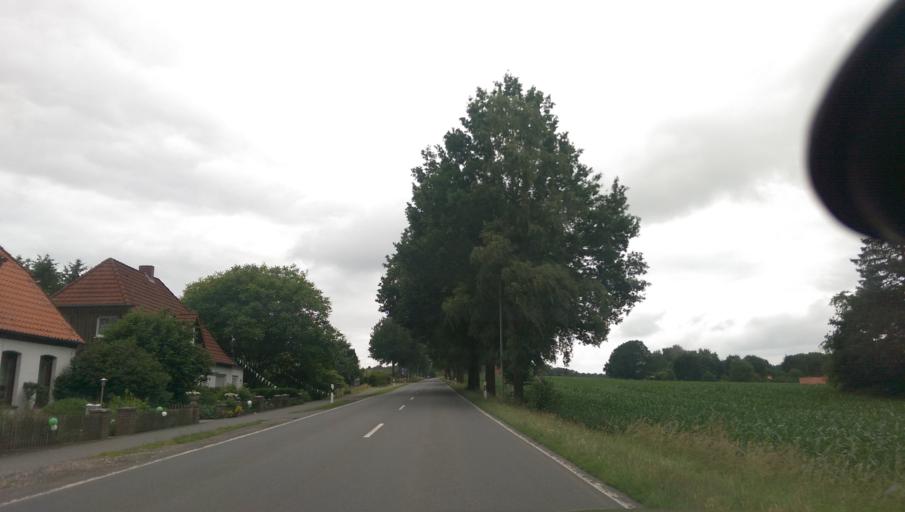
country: DE
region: Lower Saxony
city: Bomlitz
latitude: 52.9355
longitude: 9.6872
